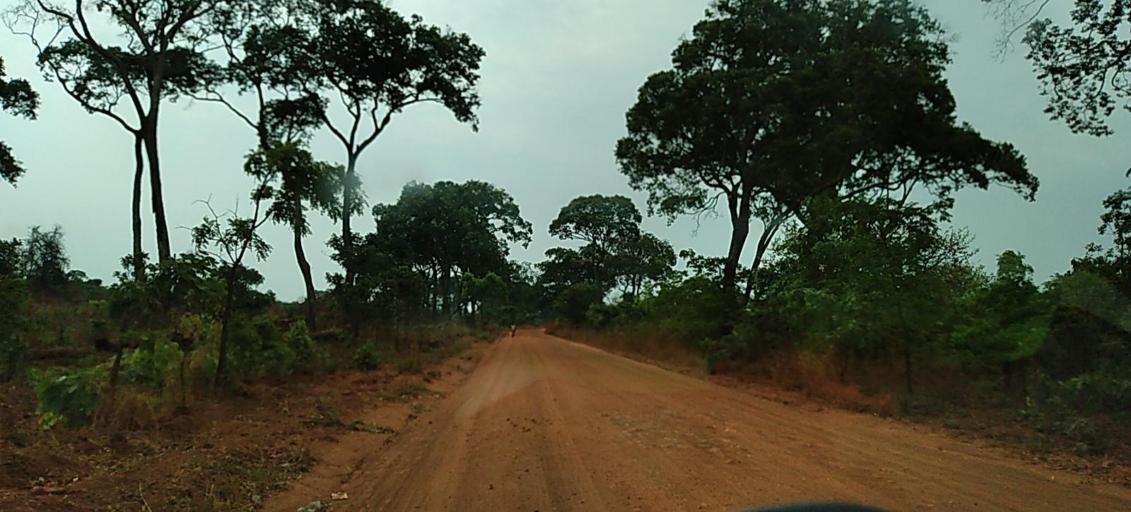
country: ZM
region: North-Western
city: Solwezi
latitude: -12.2091
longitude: 26.5006
